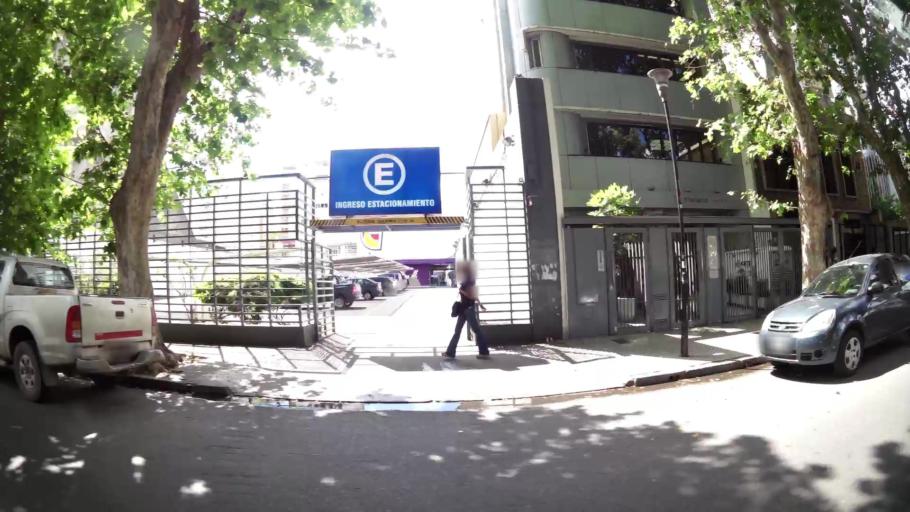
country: AR
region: Santa Fe
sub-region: Departamento de Rosario
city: Rosario
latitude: -32.9375
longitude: -60.6516
